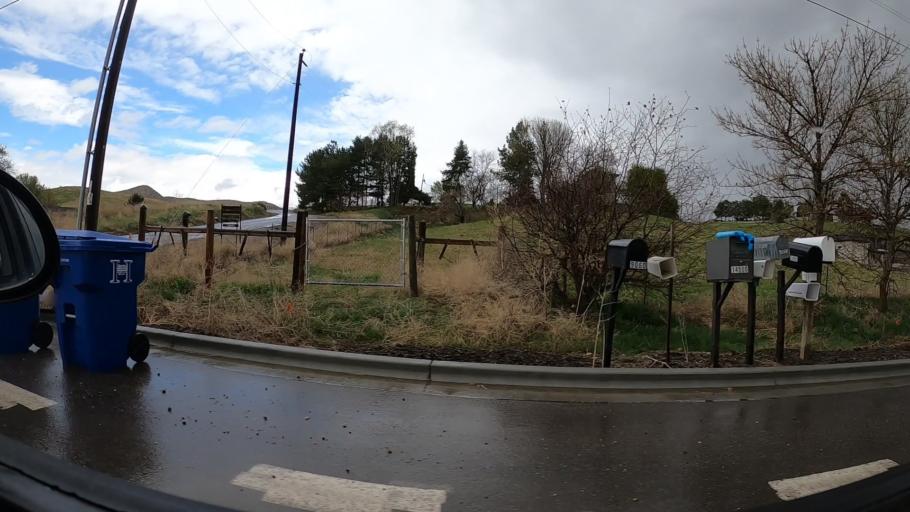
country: US
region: Idaho
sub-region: Ada County
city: Eagle
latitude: 43.7355
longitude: -116.2938
